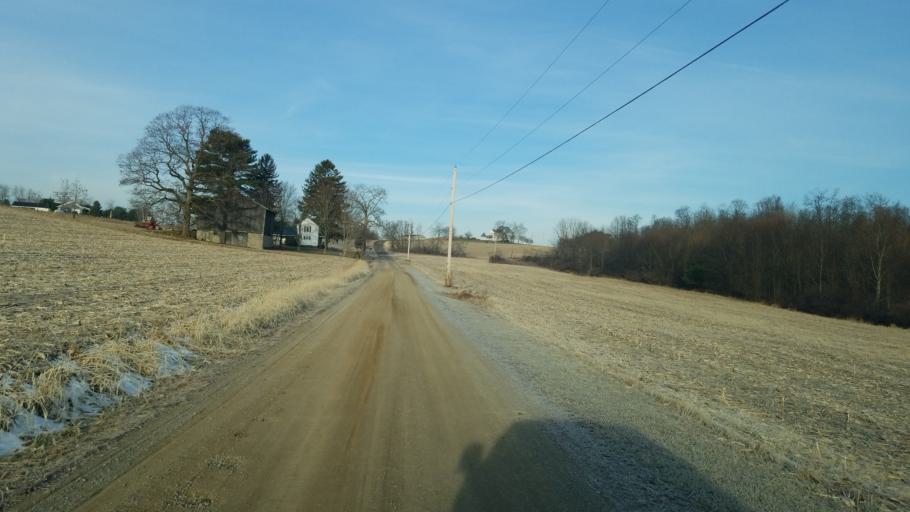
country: US
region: Pennsylvania
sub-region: Indiana County
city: Chevy Chase Heights
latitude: 40.8456
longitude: -79.2578
